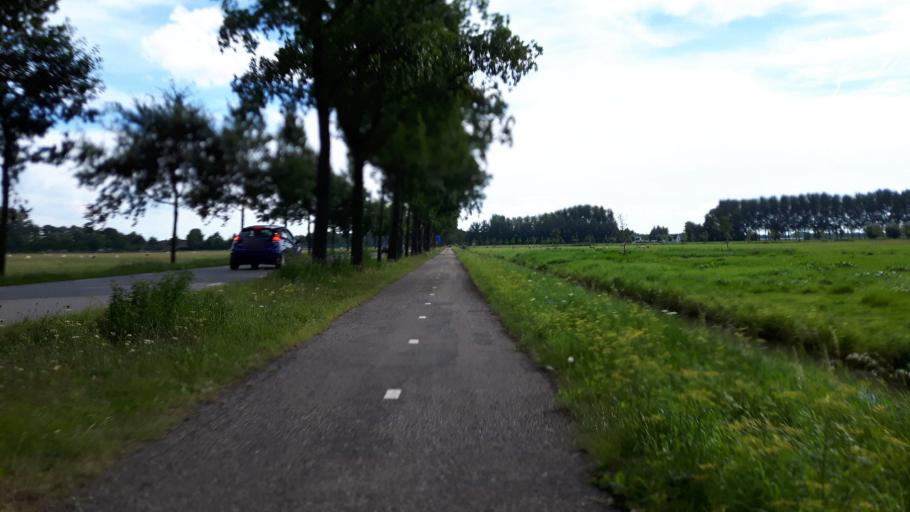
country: NL
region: Utrecht
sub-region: Stichtse Vecht
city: Spechtenkamp
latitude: 52.1184
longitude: 4.9821
